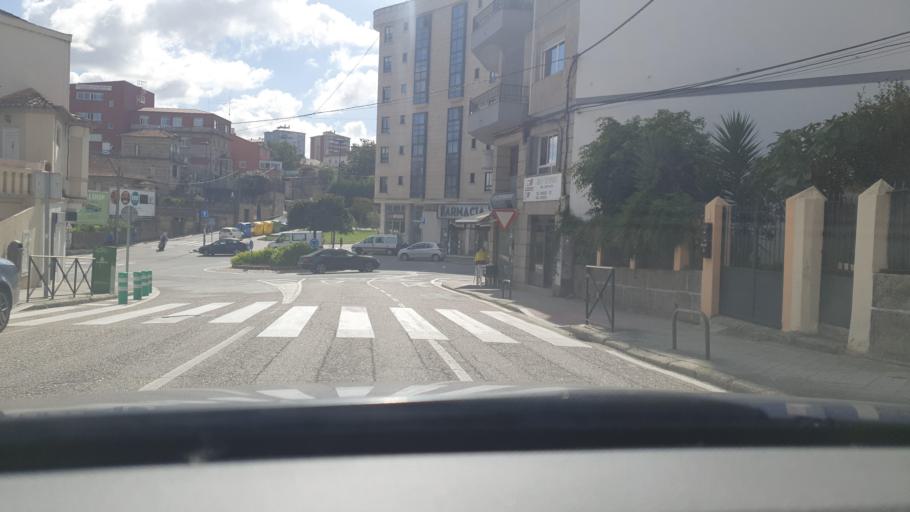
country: ES
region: Galicia
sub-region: Provincia de Pontevedra
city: Vigo
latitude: 42.2226
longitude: -8.7531
